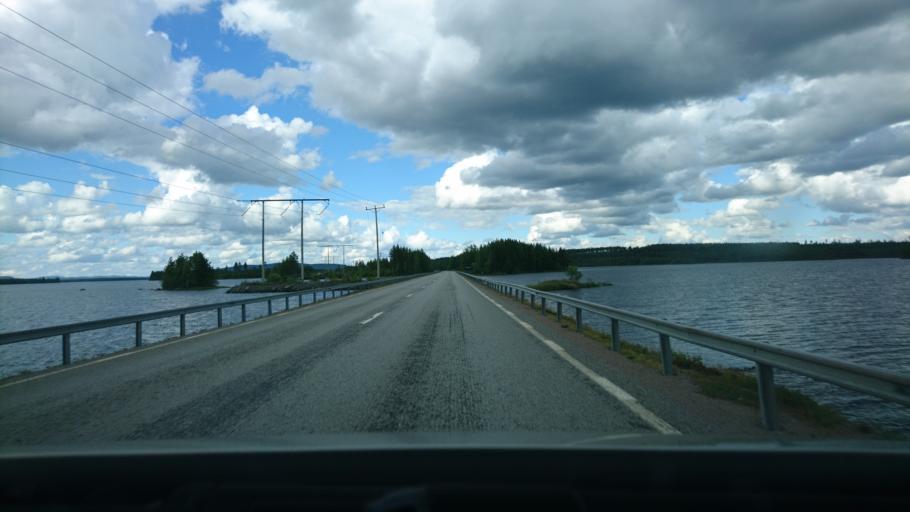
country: SE
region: Vaesterbotten
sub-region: Asele Kommun
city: Asele
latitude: 63.8913
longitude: 17.2162
